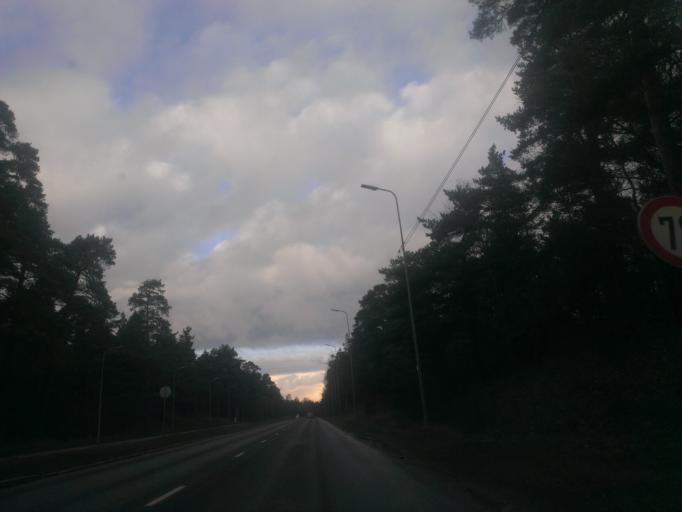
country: LV
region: Riga
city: Jaunciems
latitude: 57.0115
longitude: 24.1292
